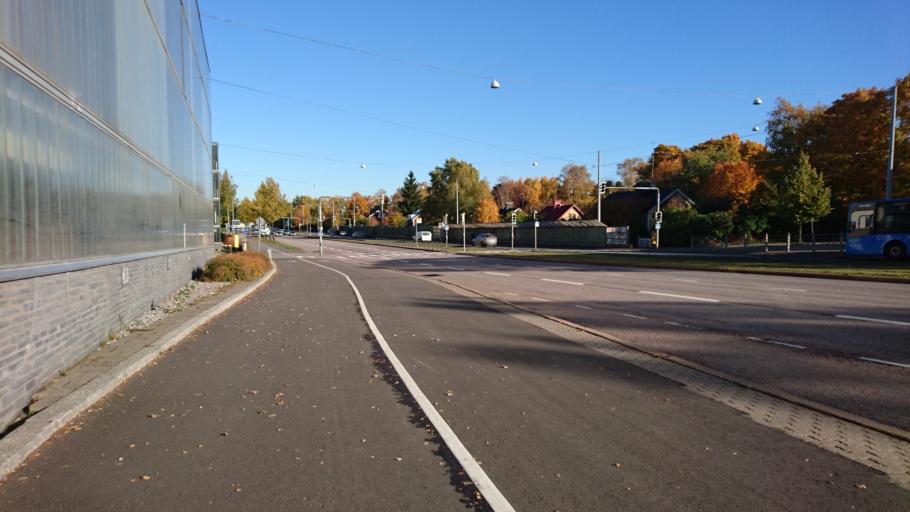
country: FI
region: Uusimaa
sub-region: Helsinki
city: Helsinki
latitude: 60.2073
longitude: 24.9675
